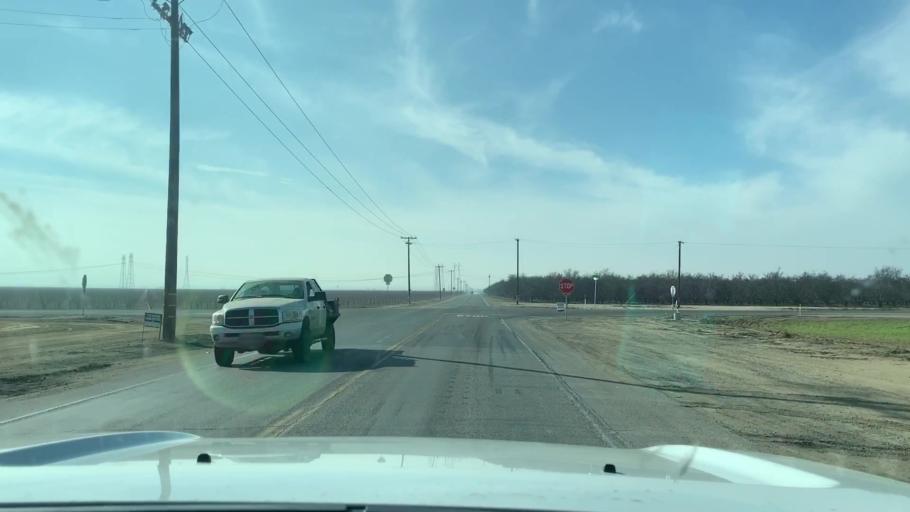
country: US
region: California
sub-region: Kern County
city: Buttonwillow
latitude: 35.4424
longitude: -119.4736
